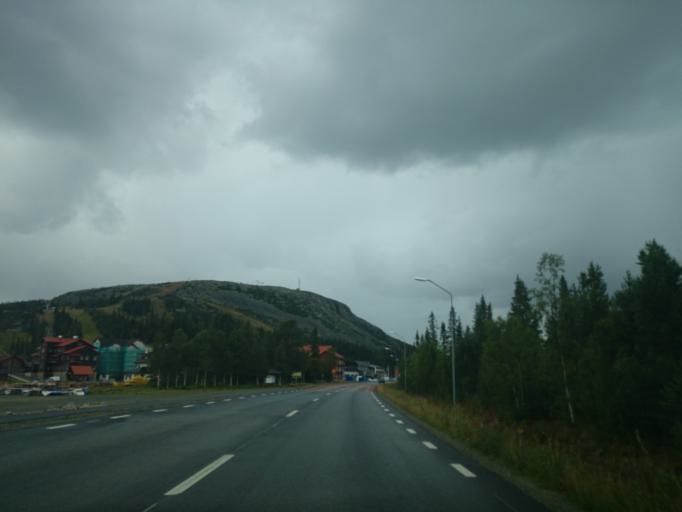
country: SE
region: Jaemtland
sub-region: Bergs Kommun
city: Hoverberg
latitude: 62.4817
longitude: 13.9792
